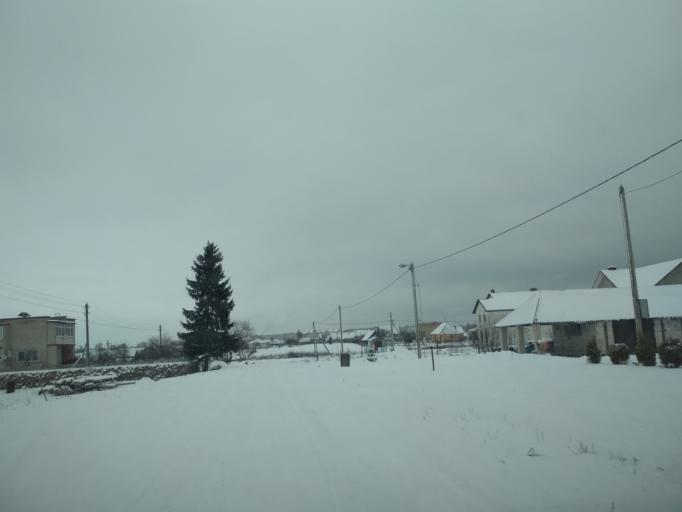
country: BY
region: Minsk
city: Mar''ina Horka
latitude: 53.5140
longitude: 28.1061
